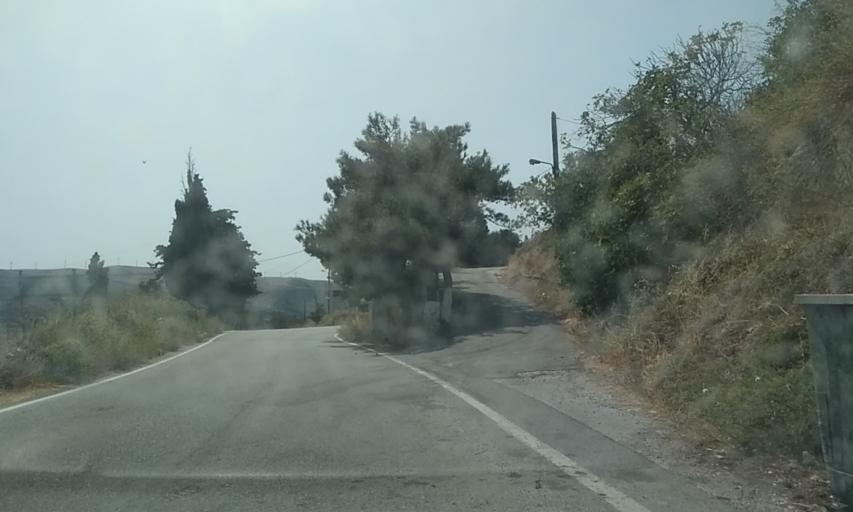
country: GR
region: Crete
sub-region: Nomos Lasithiou
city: Siteia
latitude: 35.1322
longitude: 26.0748
